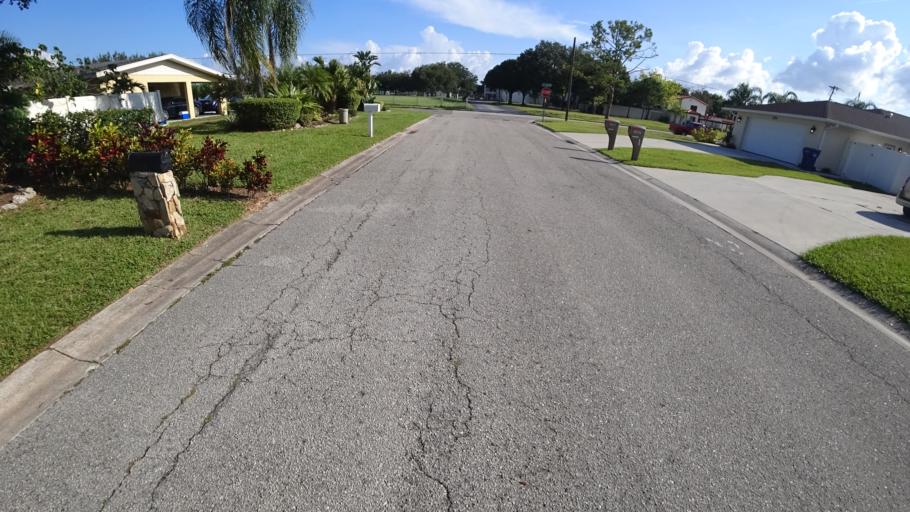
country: US
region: Florida
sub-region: Manatee County
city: South Bradenton
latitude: 27.4714
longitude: -82.5898
